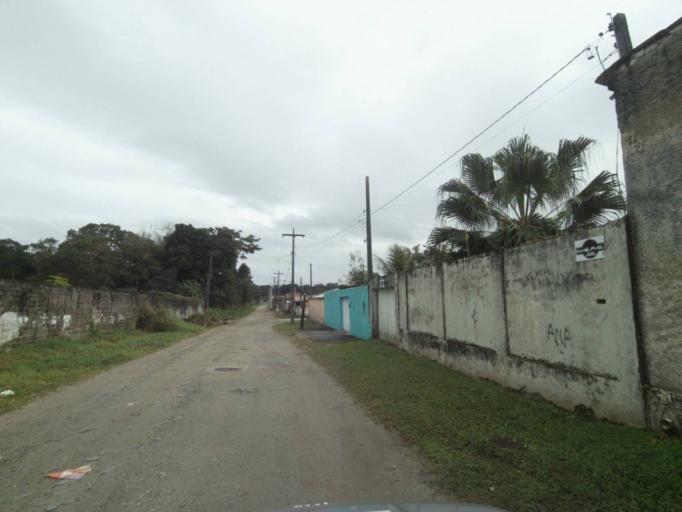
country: BR
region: Parana
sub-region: Paranagua
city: Paranagua
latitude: -25.5688
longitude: -48.5740
